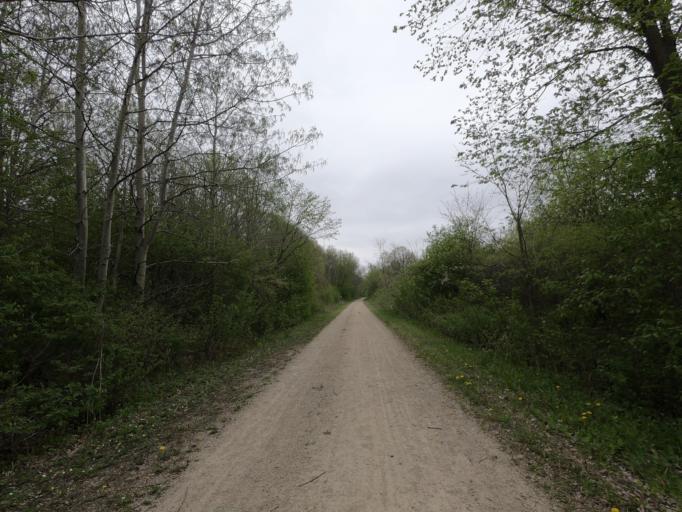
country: US
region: Wisconsin
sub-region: Jefferson County
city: Johnson Creek
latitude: 43.0354
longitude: -88.7578
